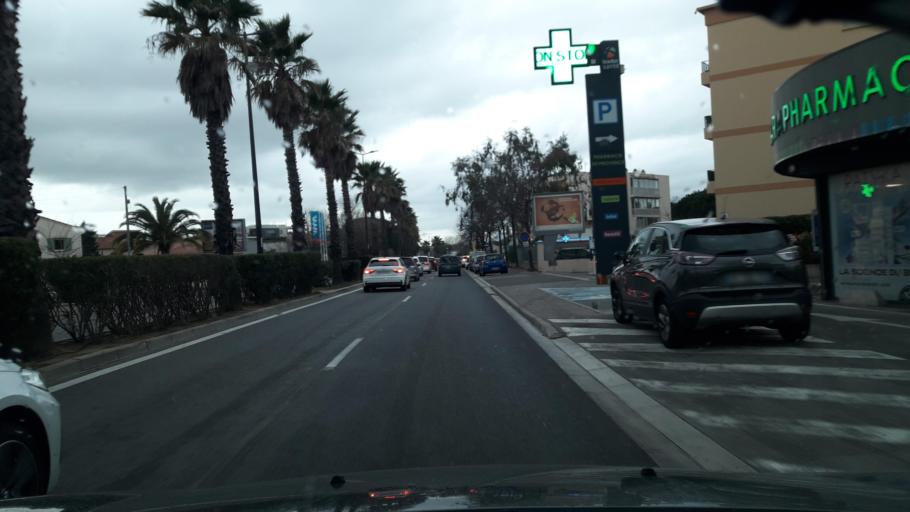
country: FR
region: Provence-Alpes-Cote d'Azur
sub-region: Departement du Var
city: Frejus
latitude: 43.4277
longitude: 6.7447
